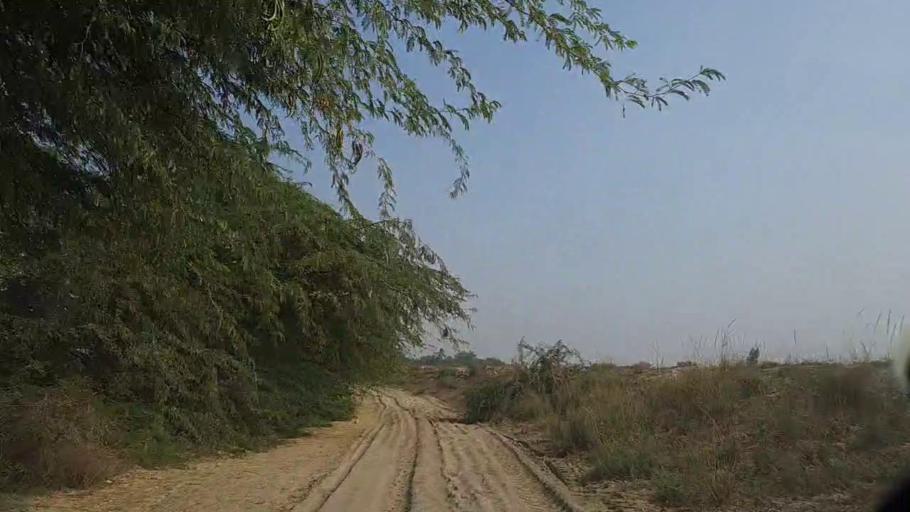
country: PK
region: Sindh
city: Thatta
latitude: 24.6534
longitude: 67.9239
